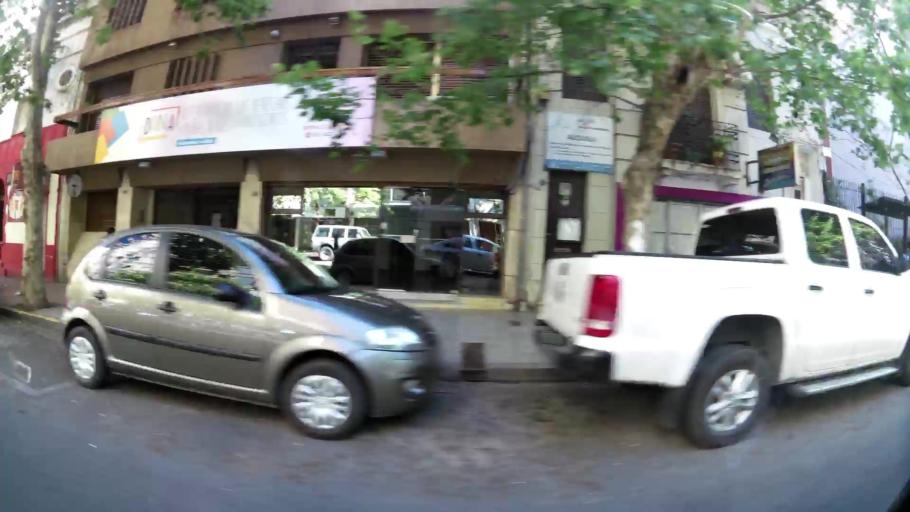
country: AR
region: Cordoba
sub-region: Departamento de Capital
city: Cordoba
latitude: -31.4233
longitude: -64.1819
